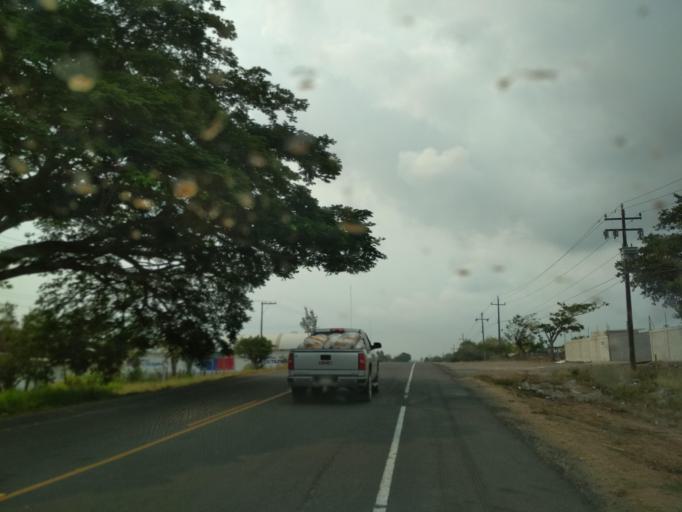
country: MX
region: Veracruz
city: Paso del Toro
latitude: 19.0100
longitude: -96.1180
